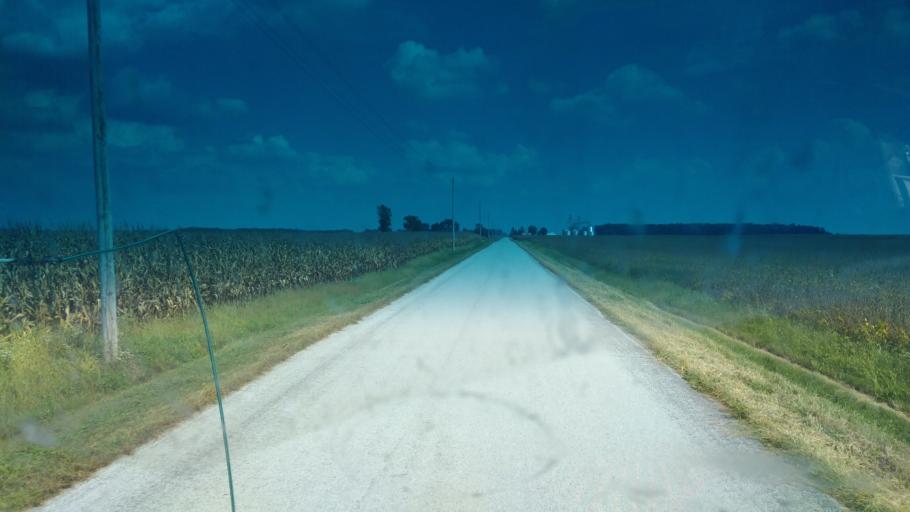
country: US
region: Ohio
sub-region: Hardin County
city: Kenton
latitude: 40.6588
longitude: -83.7228
